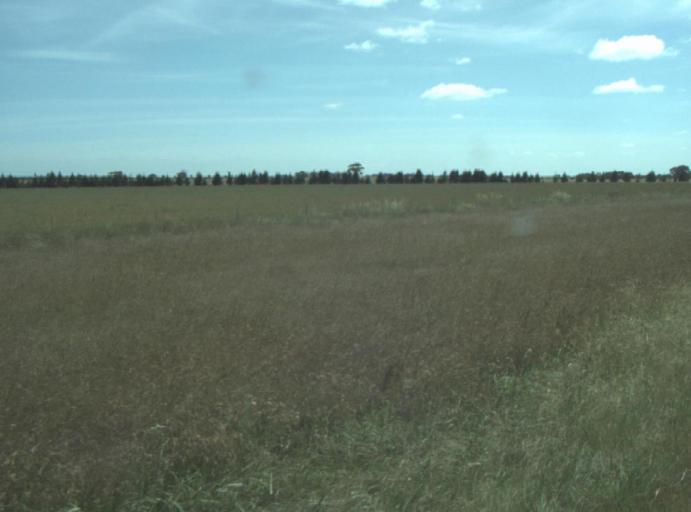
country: AU
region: Victoria
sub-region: Wyndham
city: Little River
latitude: -38.0041
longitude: 144.4679
